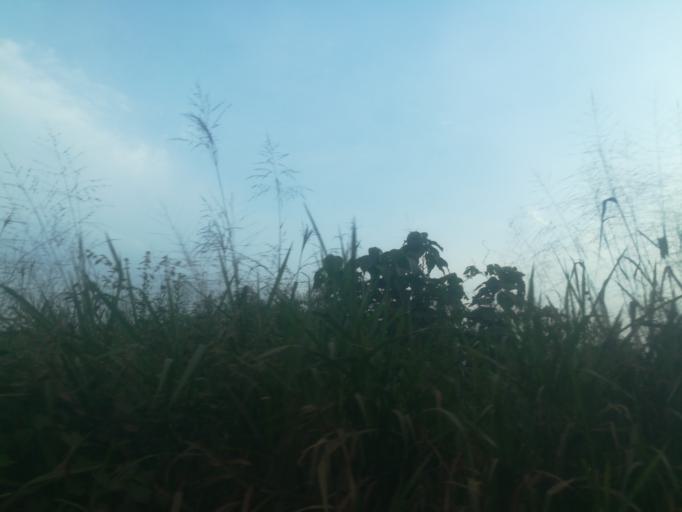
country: NG
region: Ogun
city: Abeokuta
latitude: 7.1405
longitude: 3.2610
